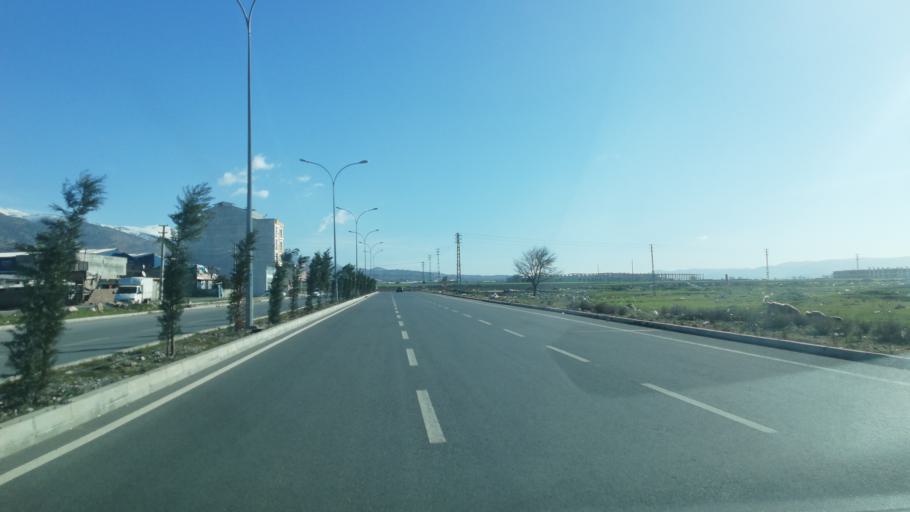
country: TR
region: Kahramanmaras
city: Kahramanmaras
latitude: 37.5711
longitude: 36.9723
